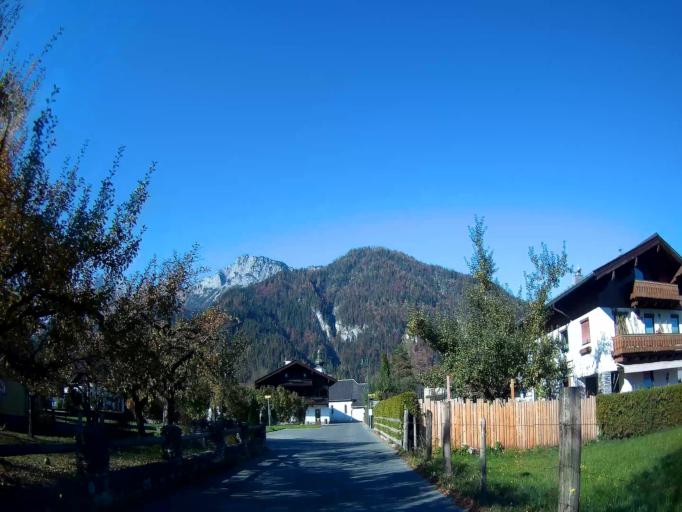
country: AT
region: Salzburg
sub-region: Politischer Bezirk Zell am See
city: Saalfelden am Steinernen Meer
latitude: 47.4466
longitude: 12.8162
